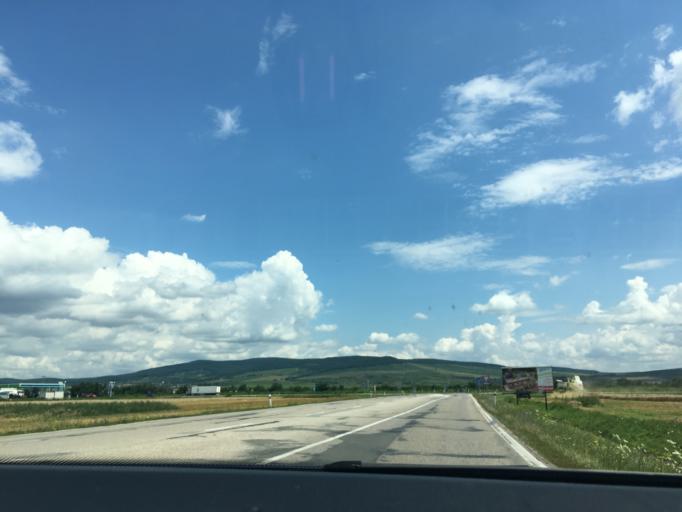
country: HU
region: Borsod-Abauj-Zemplen
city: Satoraljaujhely
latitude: 48.4256
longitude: 21.6578
